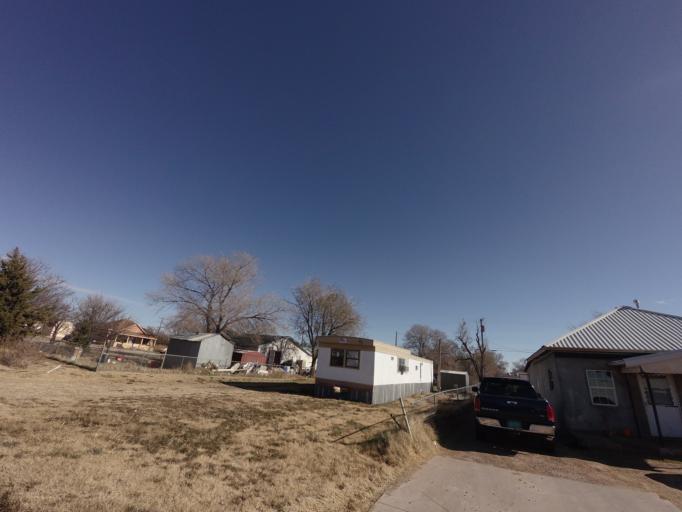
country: US
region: New Mexico
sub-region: Curry County
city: Clovis
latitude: 34.3993
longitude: -103.2129
